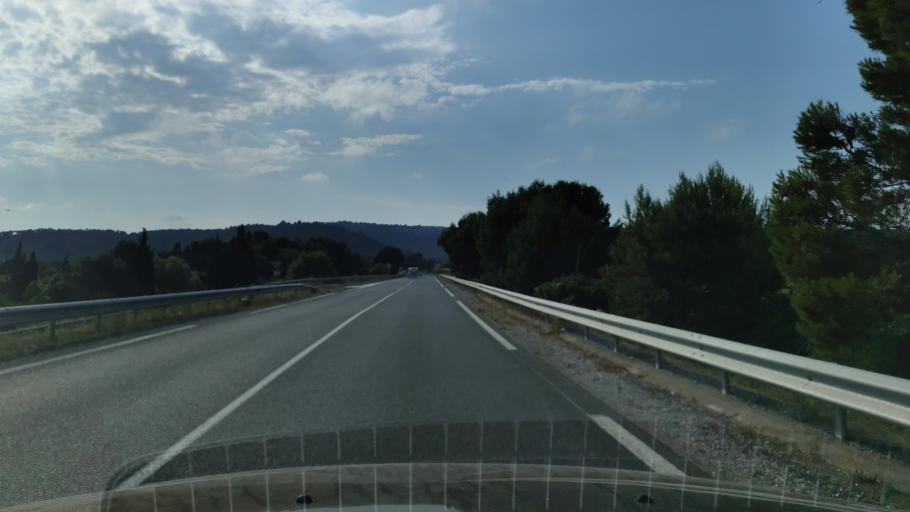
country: FR
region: Languedoc-Roussillon
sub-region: Departement de l'Aude
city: Gruissan
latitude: 43.1189
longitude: 3.1041
